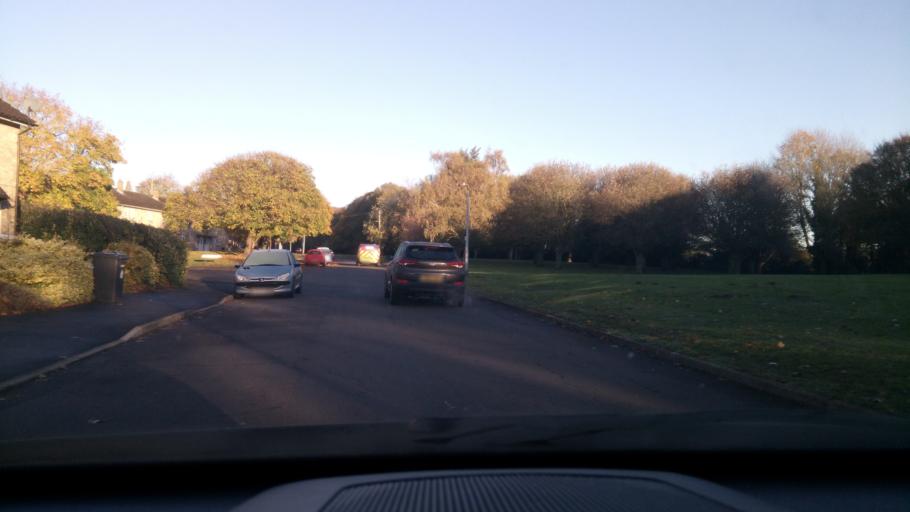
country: GB
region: England
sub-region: Peterborough
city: Wittering
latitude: 52.6084
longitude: -0.4344
